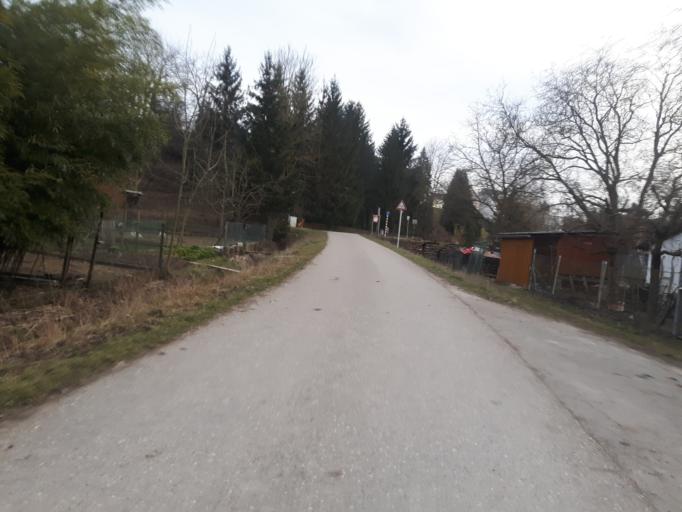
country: DE
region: Baden-Wuerttemberg
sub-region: Regierungsbezirk Stuttgart
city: Oedheim
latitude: 49.2437
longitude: 9.2590
